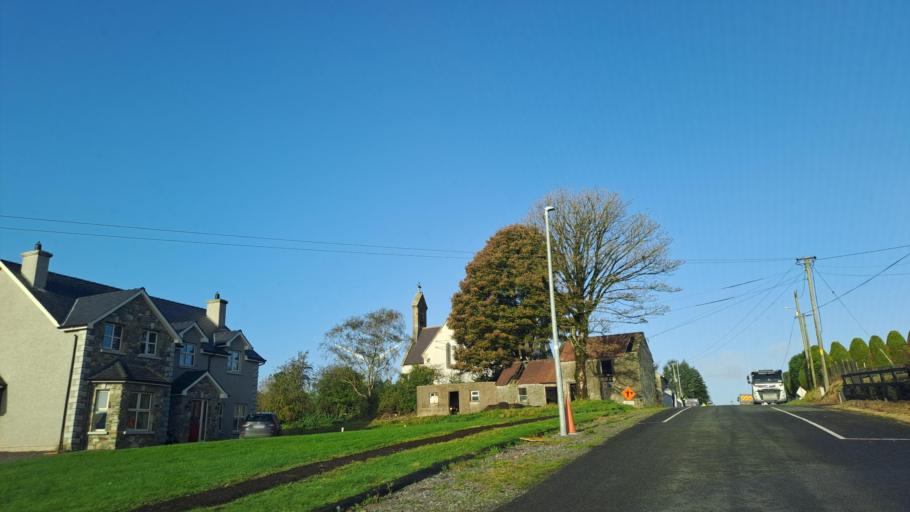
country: IE
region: Ulster
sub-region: County Monaghan
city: Castleblayney
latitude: 54.0852
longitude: -6.8601
